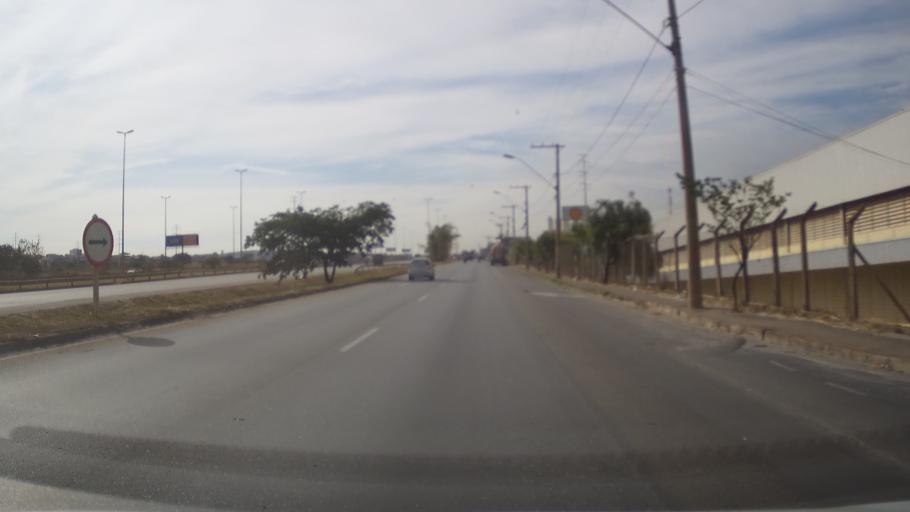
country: BR
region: Minas Gerais
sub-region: Contagem
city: Contagem
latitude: -19.9072
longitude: -44.0465
